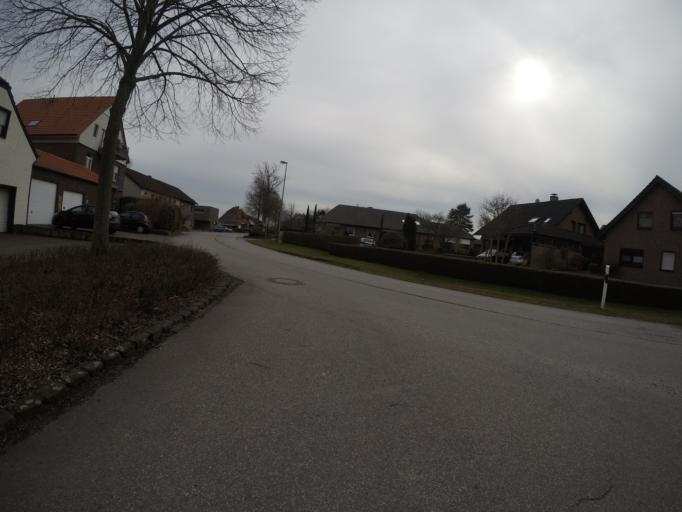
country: DE
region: North Rhine-Westphalia
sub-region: Regierungsbezirk Dusseldorf
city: Hamminkeln
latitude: 51.7730
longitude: 6.5681
